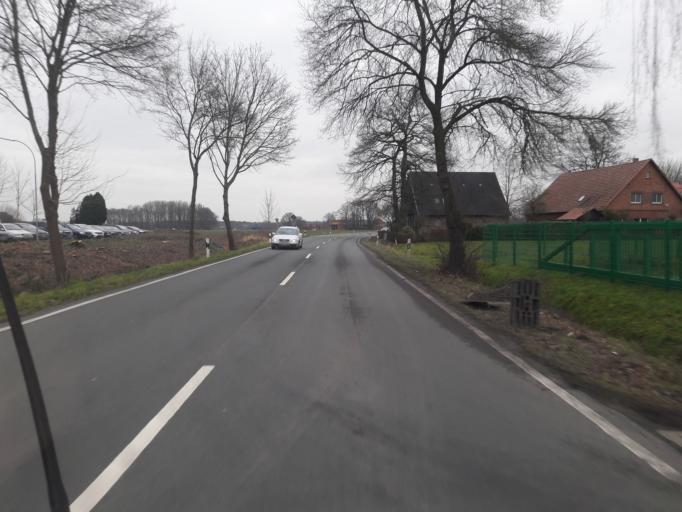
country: DE
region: Lower Saxony
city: Warmsen
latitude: 52.3807
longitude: 8.8476
